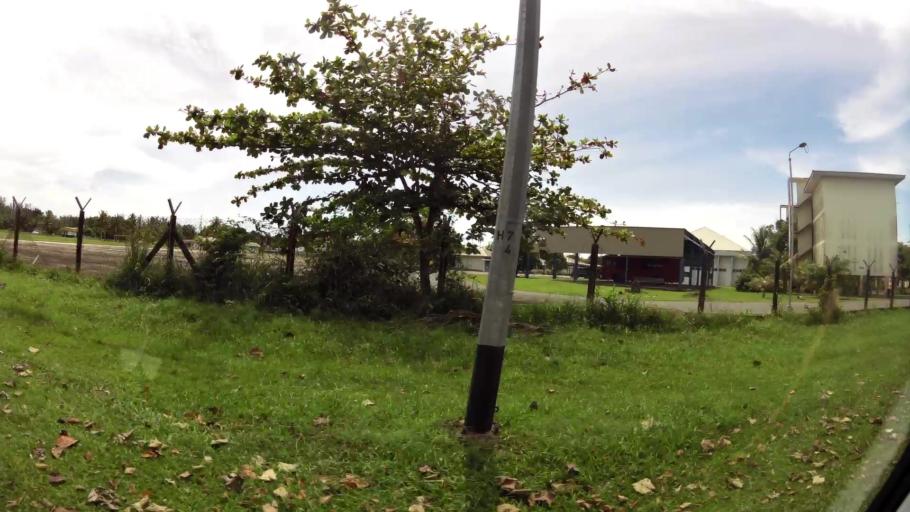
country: BN
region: Belait
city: Seria
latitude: 4.5983
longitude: 114.2827
